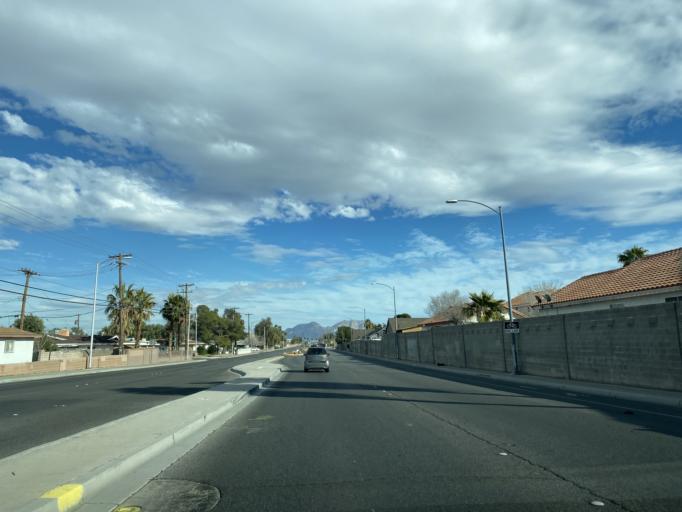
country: US
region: Nevada
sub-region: Clark County
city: Las Vegas
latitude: 36.1884
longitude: -115.1745
